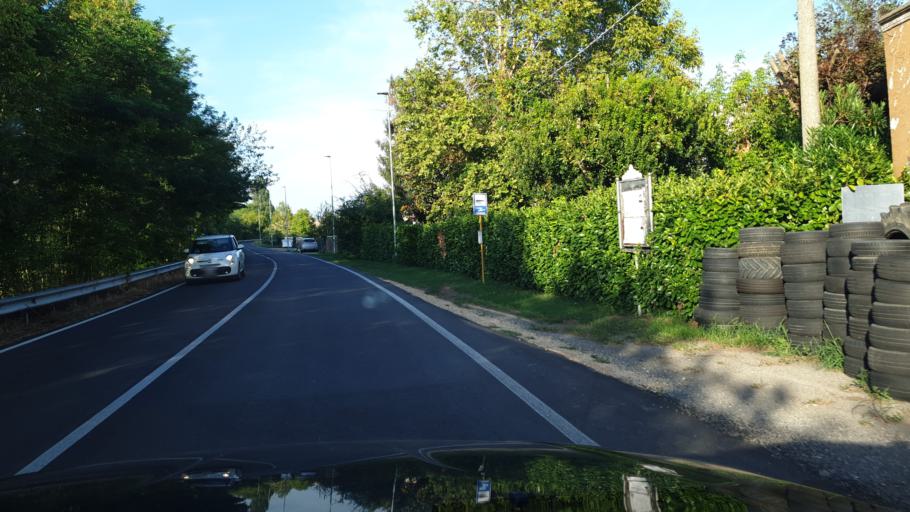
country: IT
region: Veneto
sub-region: Provincia di Rovigo
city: Pincara
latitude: 45.0011
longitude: 11.6228
